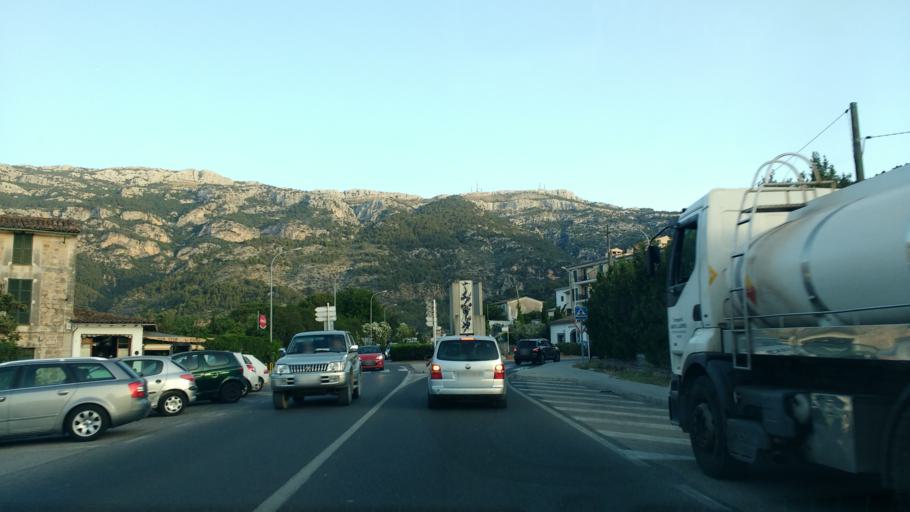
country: ES
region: Balearic Islands
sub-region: Illes Balears
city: Soller
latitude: 39.7716
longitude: 2.7060
